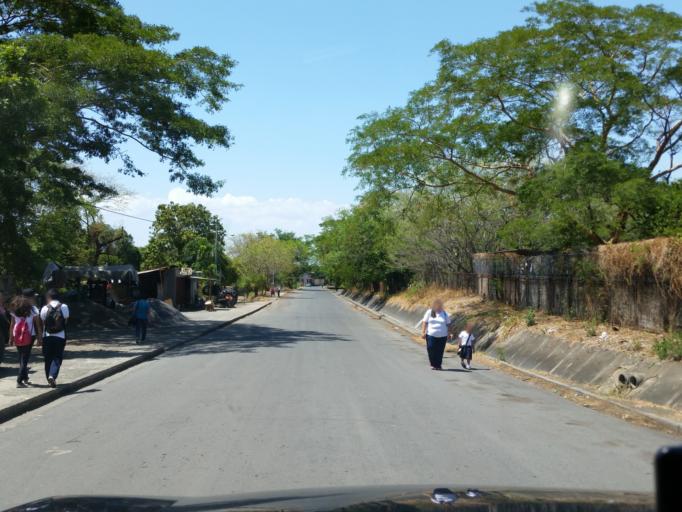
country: NI
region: Managua
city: Managua
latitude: 12.1249
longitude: -86.2780
